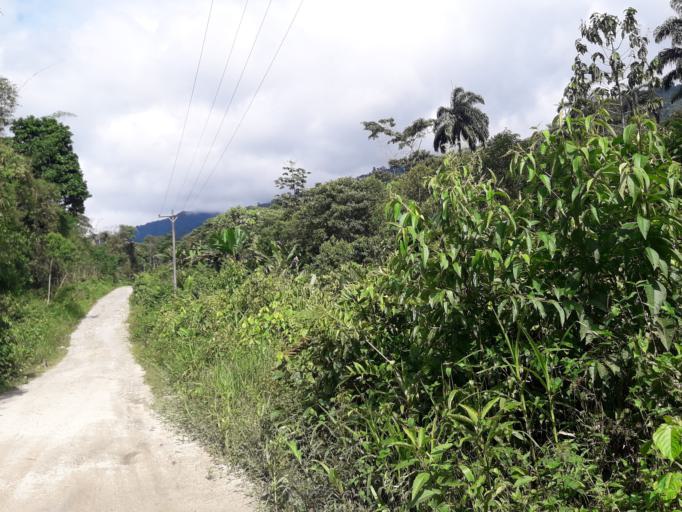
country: EC
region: Napo
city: Archidona
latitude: -0.9417
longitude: -77.8817
